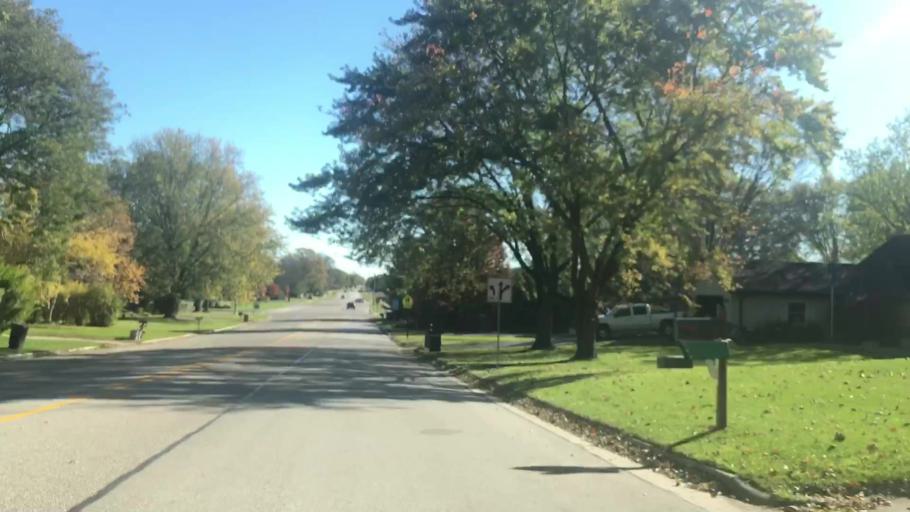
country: US
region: Wisconsin
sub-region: Waukesha County
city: Menomonee Falls
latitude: 43.1701
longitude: -88.1354
